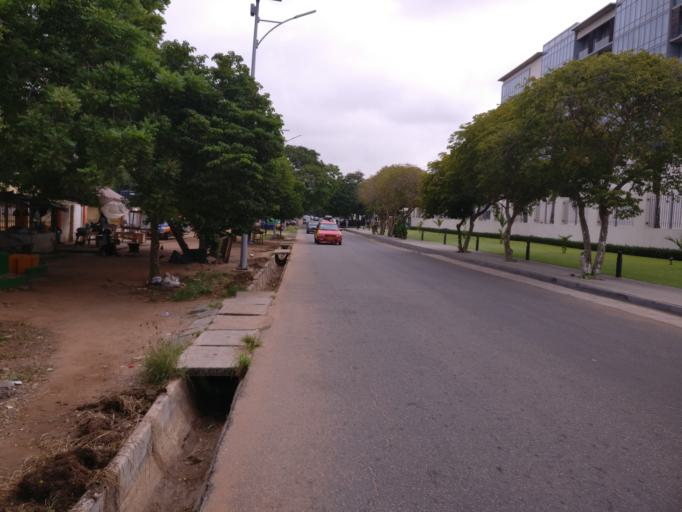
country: GH
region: Greater Accra
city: Accra
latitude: 5.5541
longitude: -0.1986
